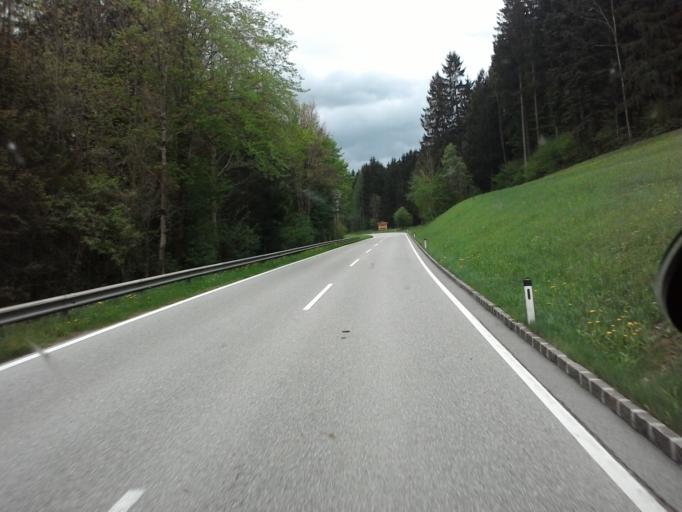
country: AT
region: Upper Austria
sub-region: Politischer Bezirk Kirchdorf an der Krems
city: Rossleithen
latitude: 47.7416
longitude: 14.2615
